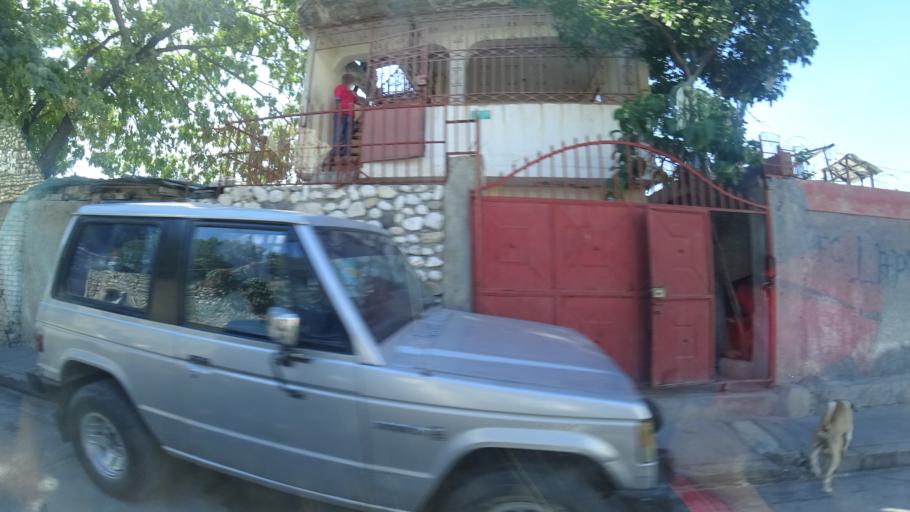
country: HT
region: Ouest
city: Delmas 73
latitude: 18.5469
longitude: -72.3150
